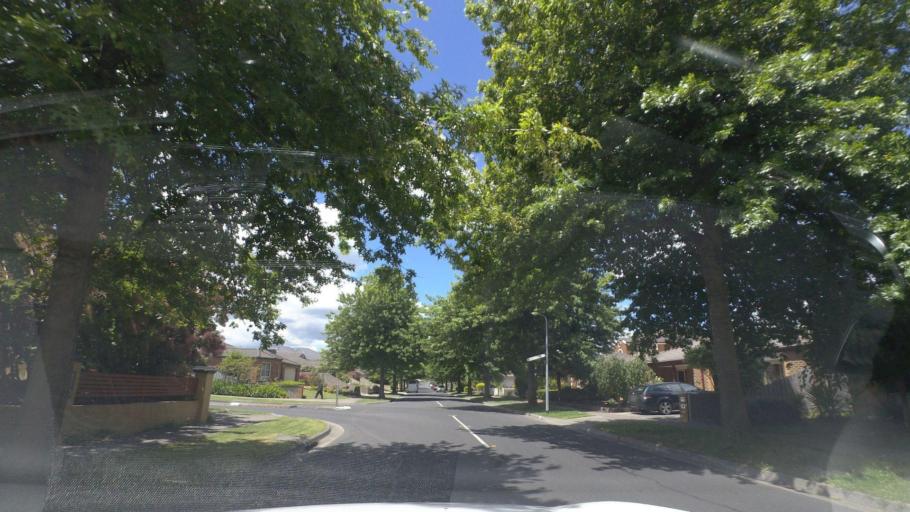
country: AU
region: Victoria
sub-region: Knox
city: Knoxfield
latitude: -37.9035
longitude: 145.2662
